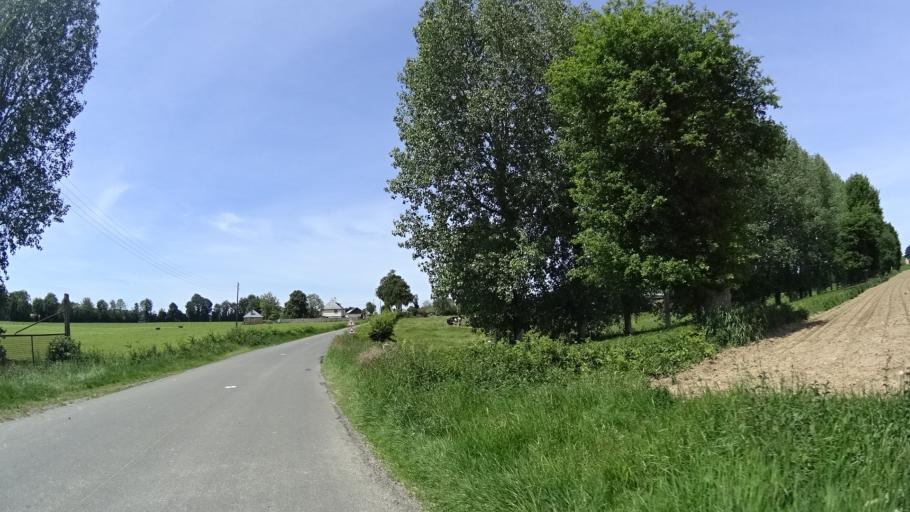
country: FR
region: Brittany
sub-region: Departement d'Ille-et-Vilaine
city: Saint-Gilles
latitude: 48.1951
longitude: -1.8436
